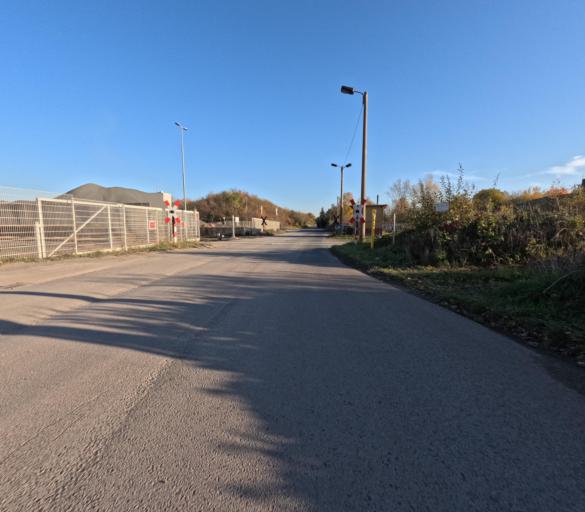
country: DE
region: Saxony
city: Otterwisch
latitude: 51.2504
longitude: 12.6494
